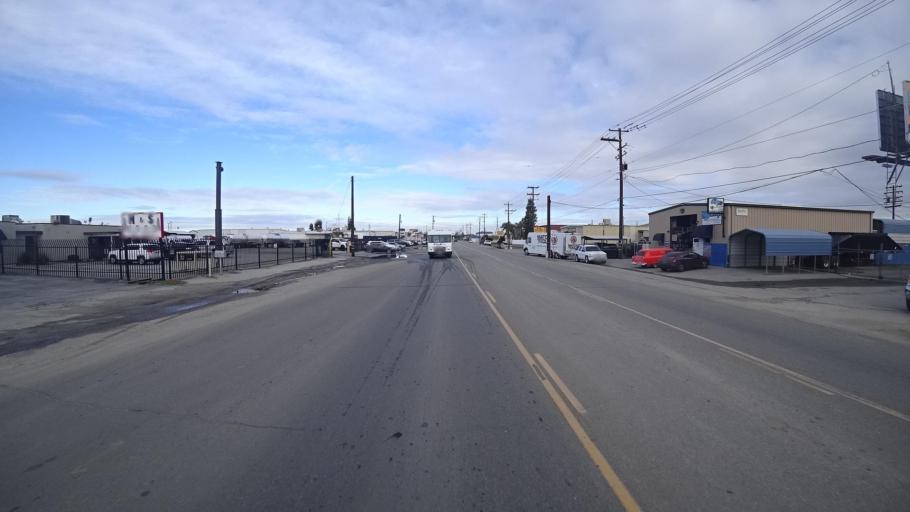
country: US
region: California
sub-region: Kern County
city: Greenacres
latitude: 35.3908
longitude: -119.0744
